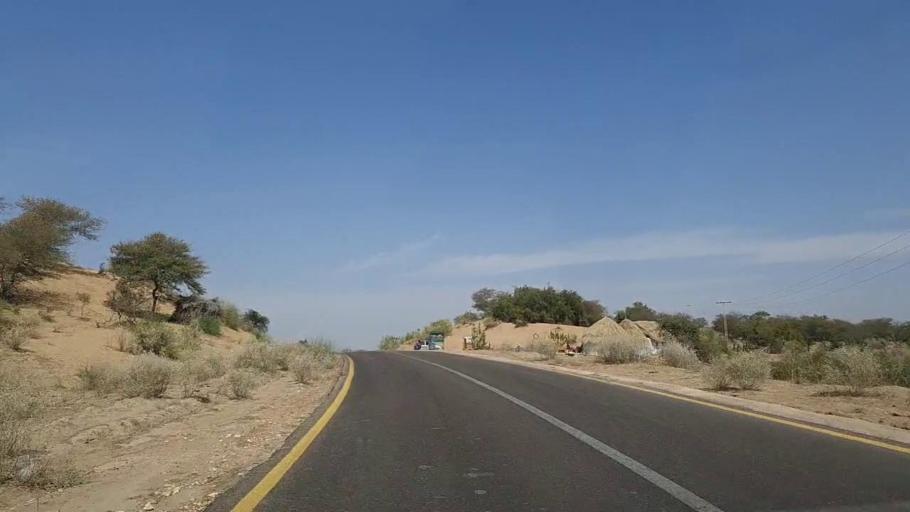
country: PK
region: Sindh
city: Mithi
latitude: 24.8977
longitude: 69.8826
